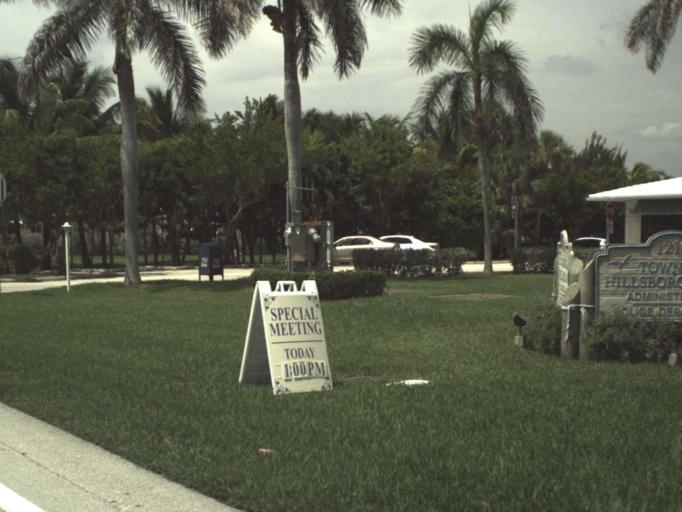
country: US
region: Florida
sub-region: Broward County
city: Hillsboro Beach
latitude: 26.3009
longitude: -80.0782
